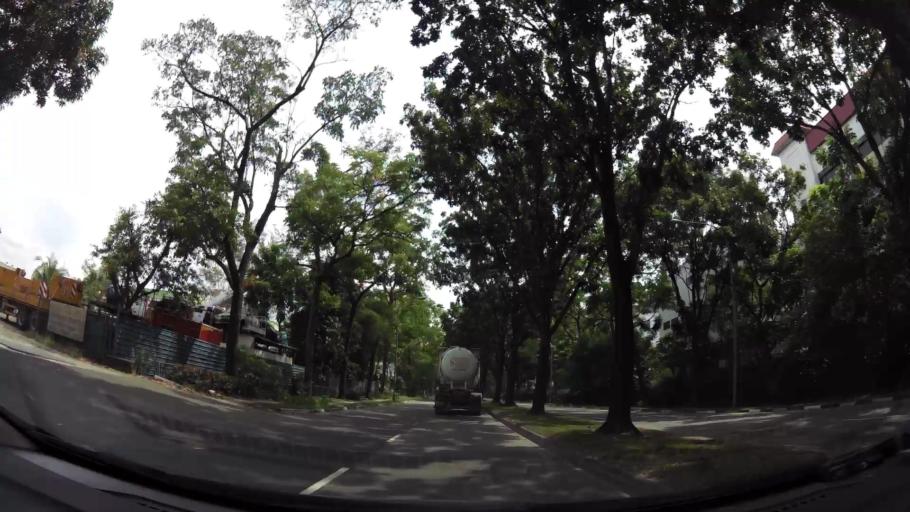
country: MY
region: Johor
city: Johor Bahru
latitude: 1.4152
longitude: 103.7444
